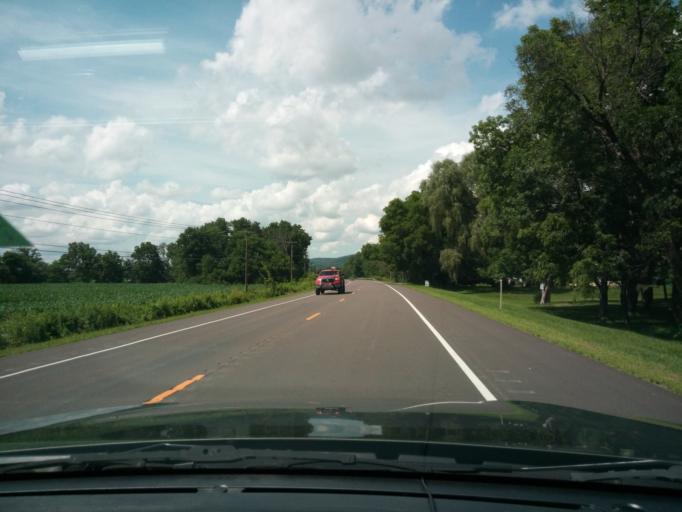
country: US
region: New York
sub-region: Chemung County
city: Southport
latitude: 42.0290
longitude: -76.7420
